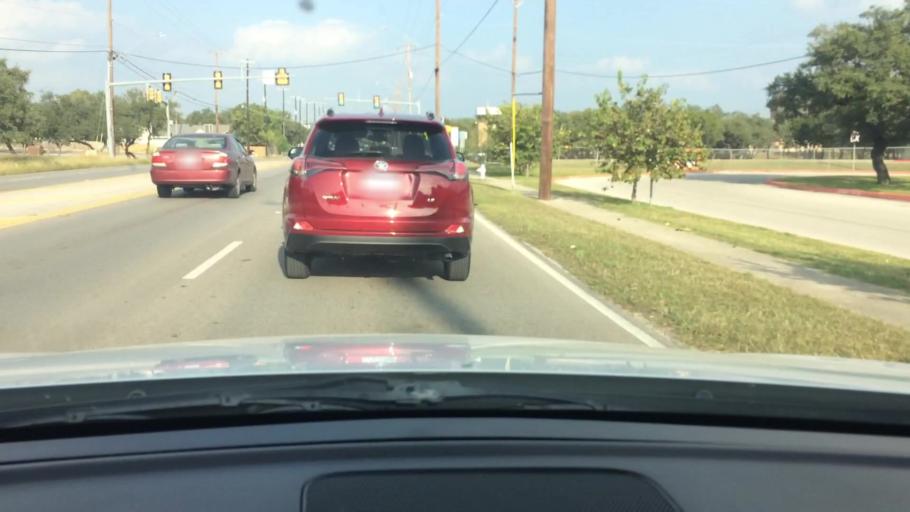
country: US
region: Texas
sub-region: Bexar County
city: Shavano Park
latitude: 29.5661
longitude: -98.5831
